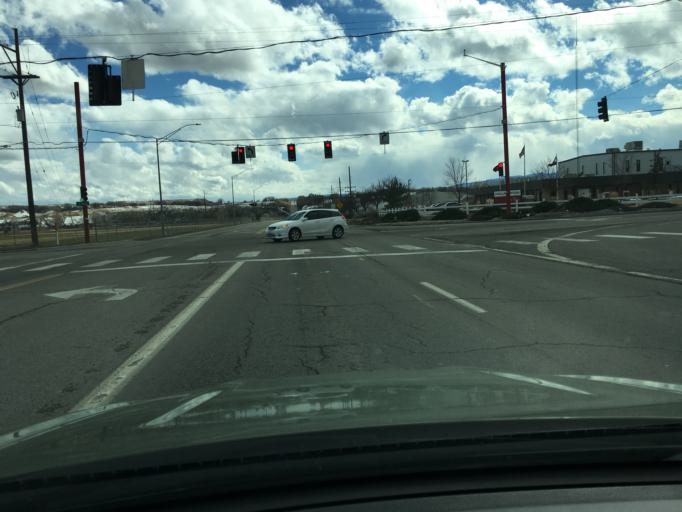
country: US
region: Colorado
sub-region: Mesa County
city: Clifton
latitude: 39.0631
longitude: -108.4595
